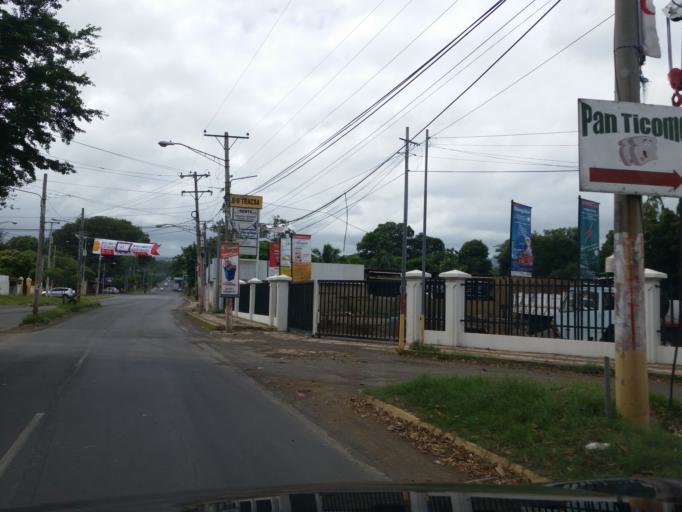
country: NI
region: Managua
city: Ciudad Sandino
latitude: 12.0952
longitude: -86.3241
